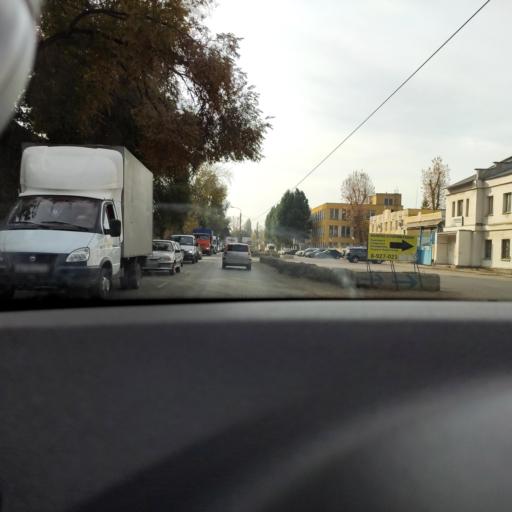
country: RU
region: Samara
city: Samara
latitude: 53.1938
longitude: 50.2456
